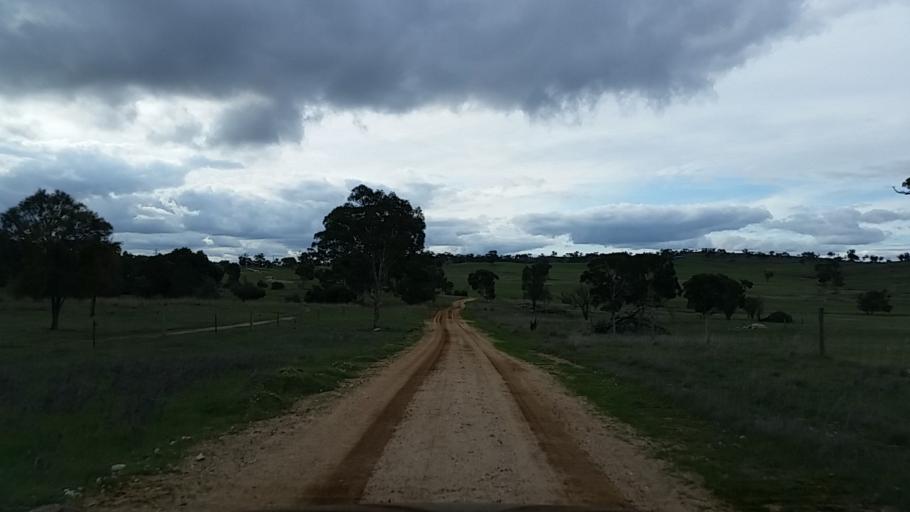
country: AU
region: South Australia
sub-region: Mount Barker
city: Callington
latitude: -34.9668
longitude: 139.0541
